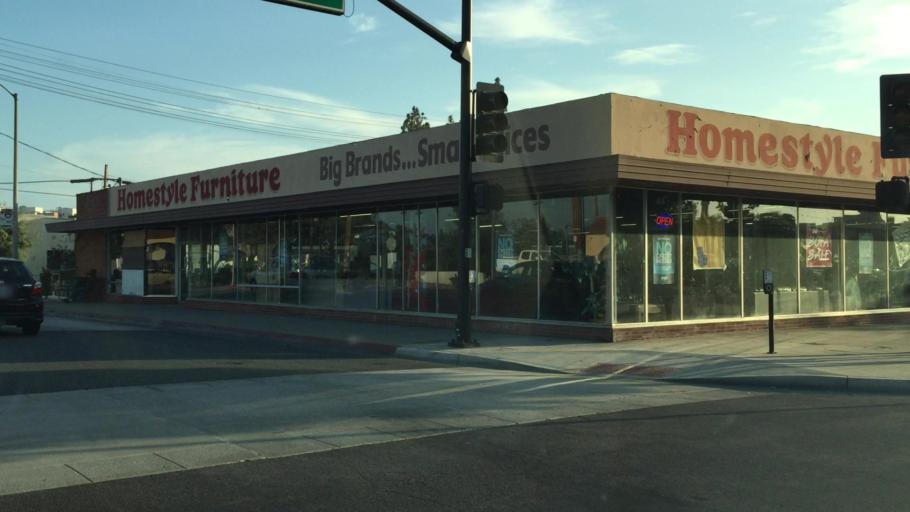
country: US
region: California
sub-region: San Diego County
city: El Cajon
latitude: 32.7949
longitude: -116.9589
